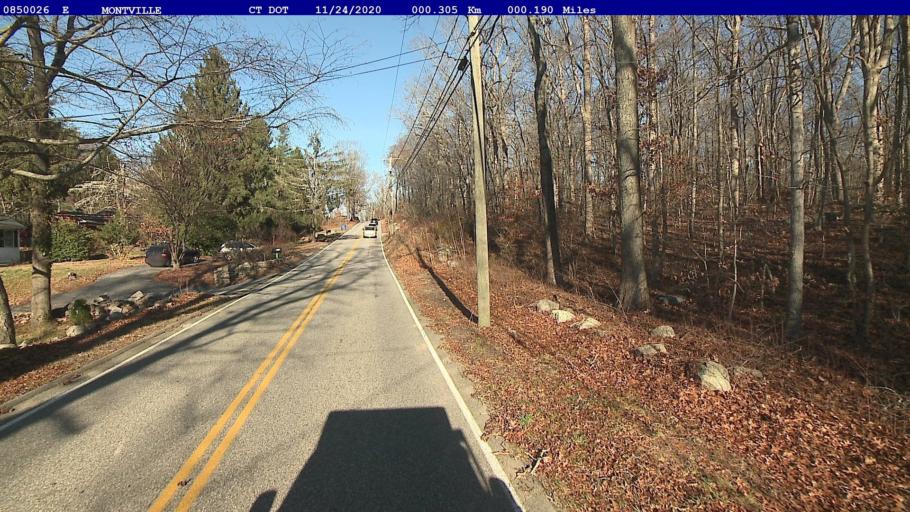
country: US
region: Connecticut
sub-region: New London County
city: Montville Center
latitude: 41.4316
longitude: -72.2154
